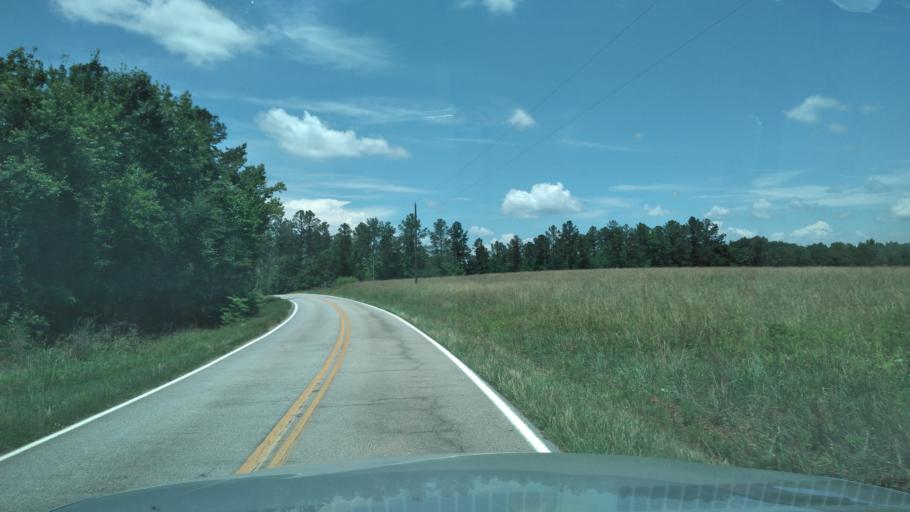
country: US
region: South Carolina
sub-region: Laurens County
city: Laurens
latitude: 34.3789
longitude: -82.0853
